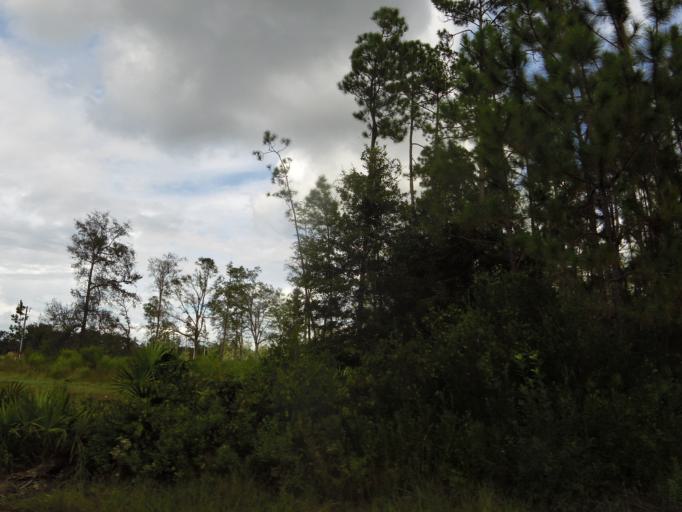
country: US
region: Florida
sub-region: Nassau County
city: Hilliard
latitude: 30.6108
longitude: -82.0783
